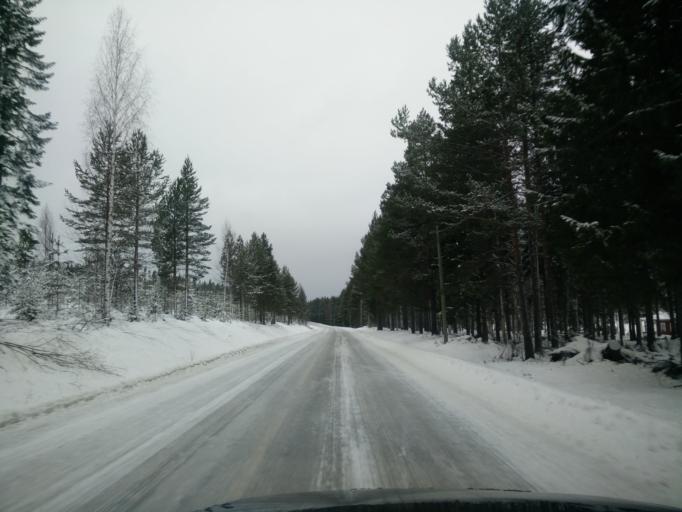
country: SE
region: Jaemtland
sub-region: Braecke Kommun
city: Braecke
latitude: 62.4048
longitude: 15.2973
